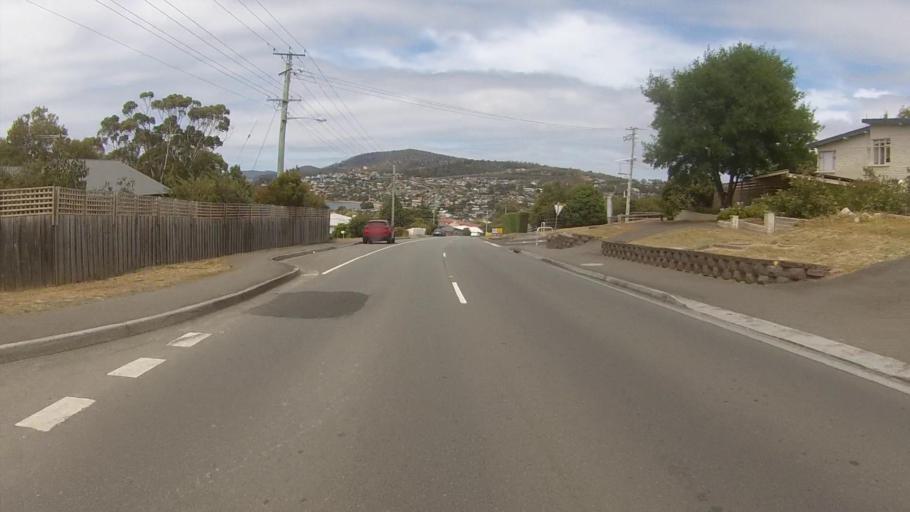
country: AU
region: Tasmania
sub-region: Kingborough
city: Blackmans Bay
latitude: -42.9942
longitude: 147.3241
